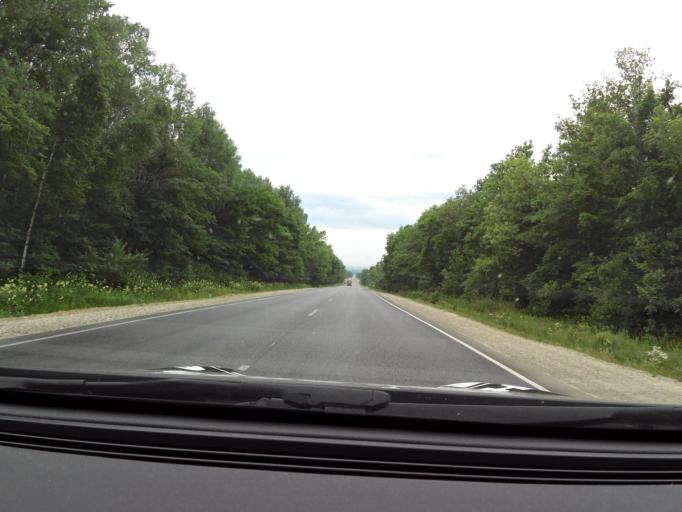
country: RU
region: Bashkortostan
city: Ulu-Telyak
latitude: 54.8400
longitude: 57.0448
